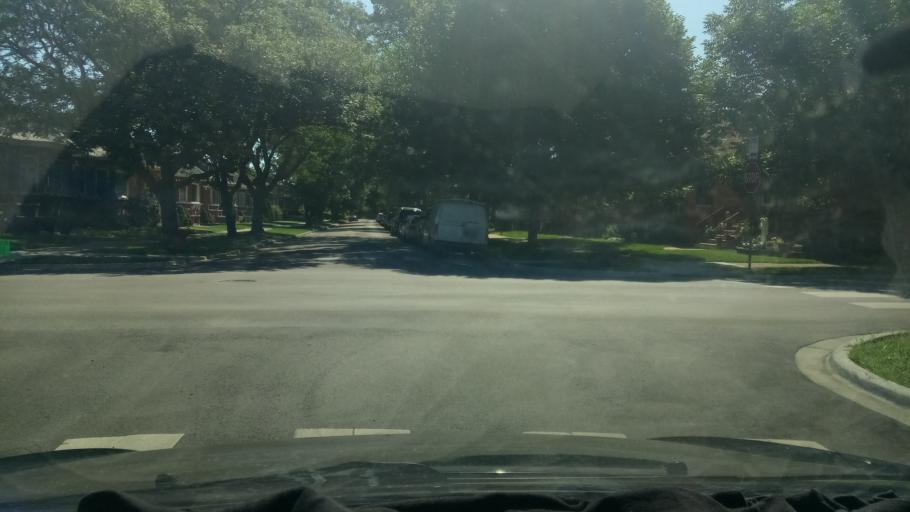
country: US
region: Illinois
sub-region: Cook County
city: Hometown
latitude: 41.7797
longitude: -87.7165
